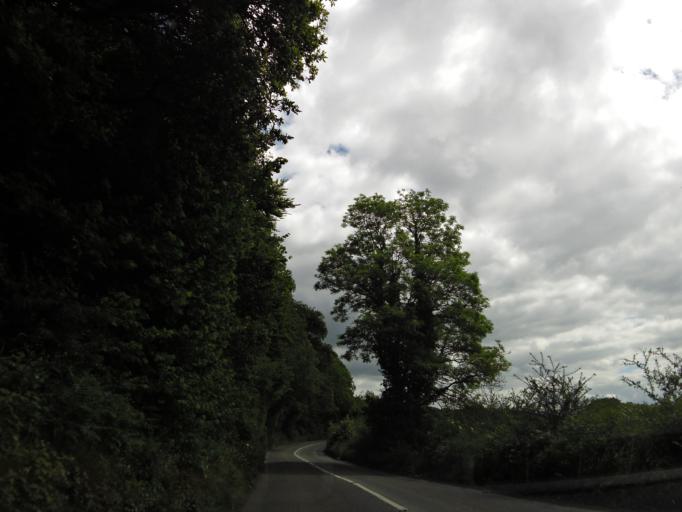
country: IE
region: Munster
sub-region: North Tipperary
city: Nenagh
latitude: 52.7936
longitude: -8.0446
